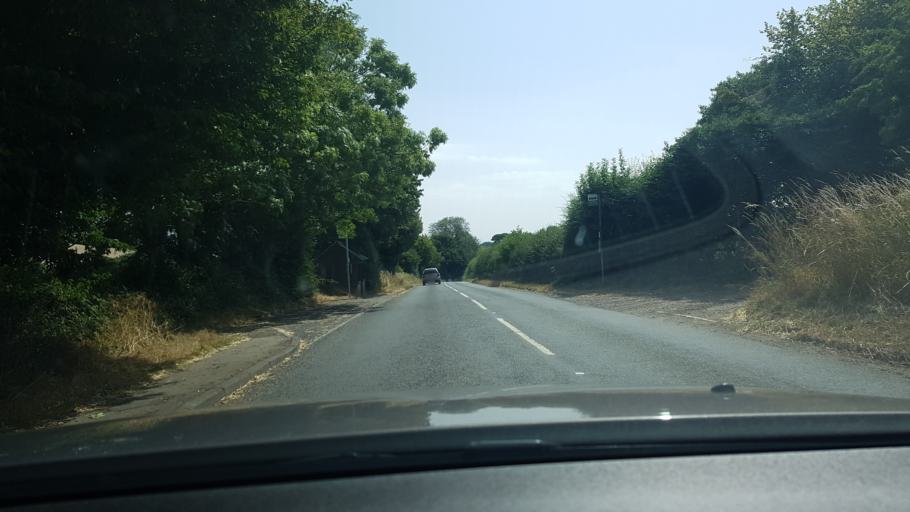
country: GB
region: England
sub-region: West Berkshire
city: Lambourn
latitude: 51.4876
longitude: -1.4786
